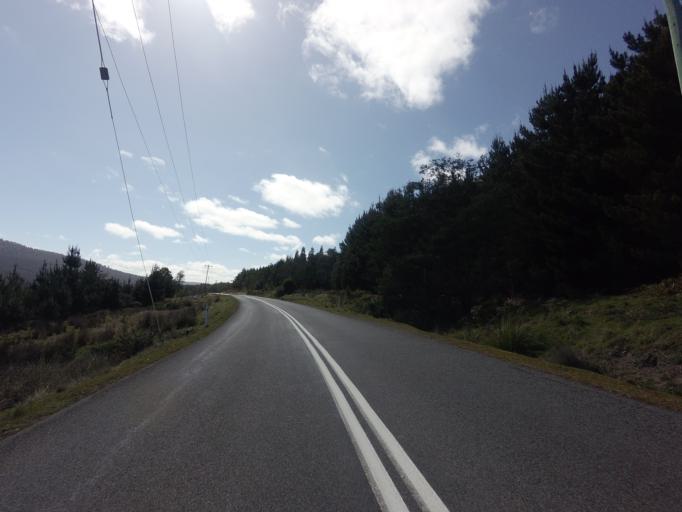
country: AU
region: Tasmania
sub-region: Derwent Valley
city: New Norfolk
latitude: -42.7436
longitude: 146.6562
